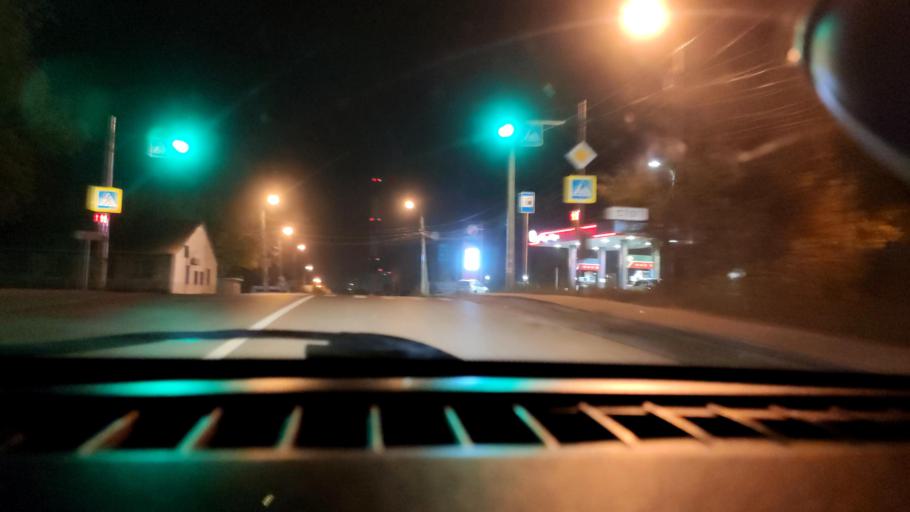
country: RU
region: Samara
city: Samara
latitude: 53.1826
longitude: 50.1634
